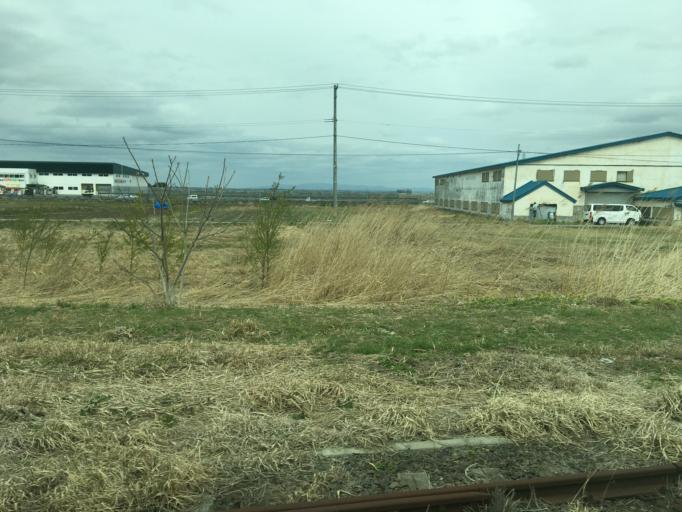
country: JP
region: Aomori
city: Shimokizukuri
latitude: 40.7820
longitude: 140.3372
